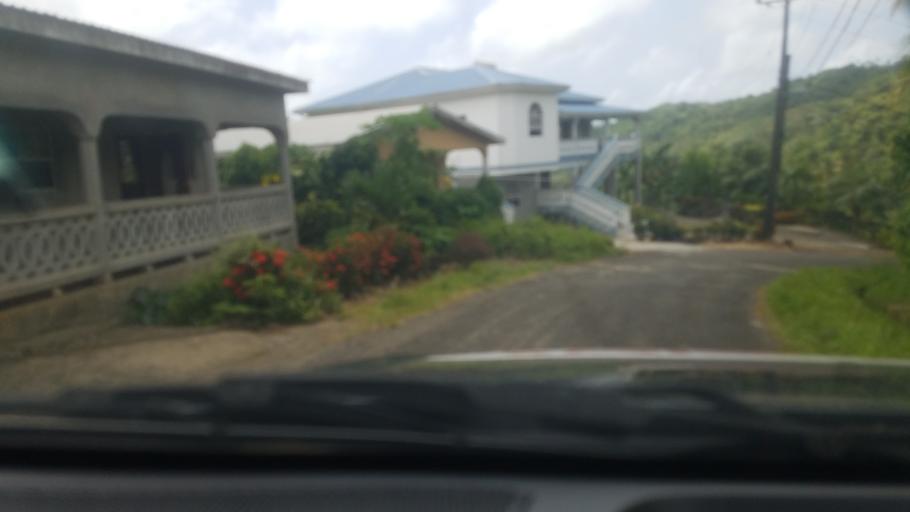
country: LC
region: Micoud Quarter
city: Micoud
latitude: 13.8007
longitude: -60.9476
